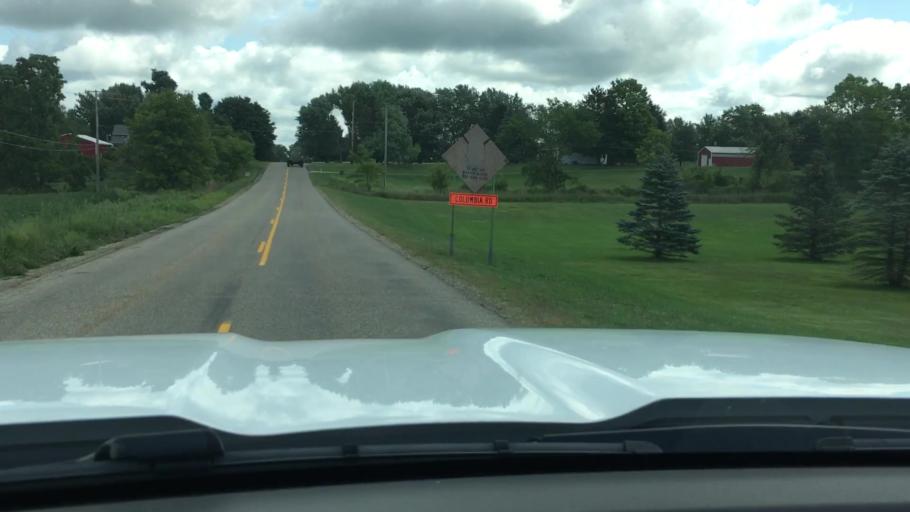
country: US
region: Michigan
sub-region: Eaton County
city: Dimondale
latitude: 42.5820
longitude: -84.6183
